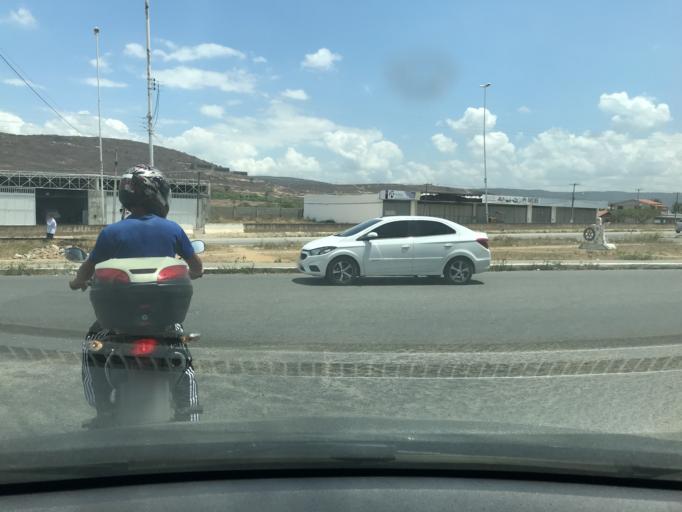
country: BR
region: Pernambuco
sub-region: Bezerros
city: Bezerros
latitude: -8.2381
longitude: -35.7452
